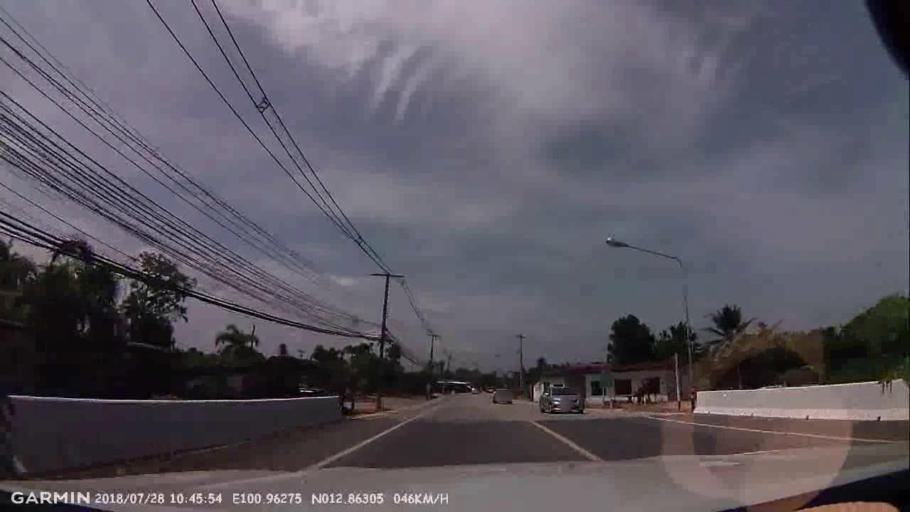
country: TH
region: Chon Buri
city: Phatthaya
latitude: 12.8630
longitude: 100.9628
